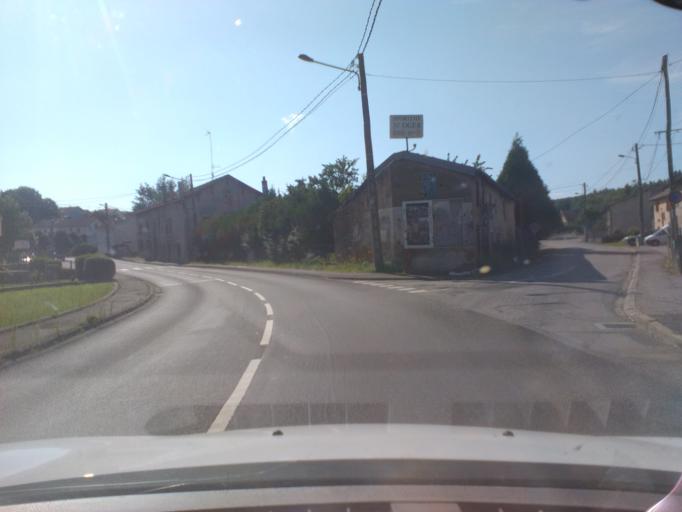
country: FR
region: Lorraine
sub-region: Departement des Vosges
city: Deyvillers
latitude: 48.1985
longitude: 6.5203
